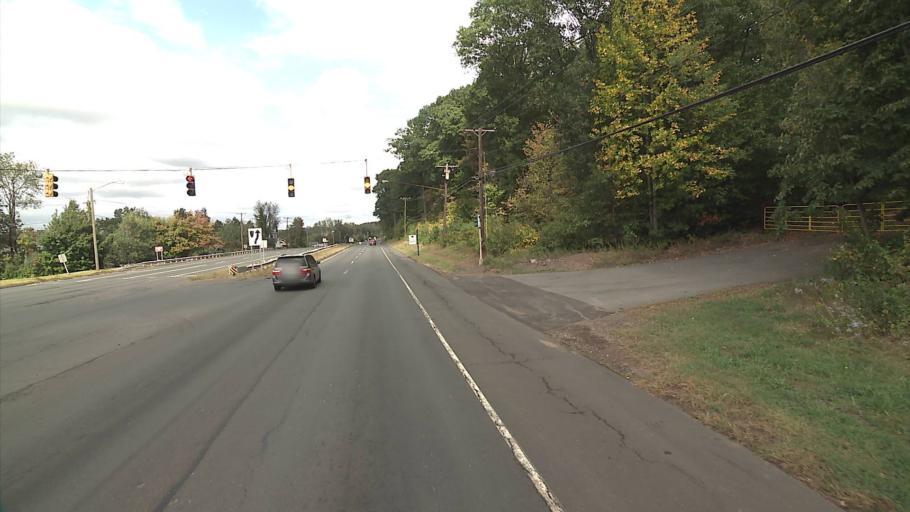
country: US
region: Connecticut
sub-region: New Haven County
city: Meriden
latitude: 41.5776
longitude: -72.7677
